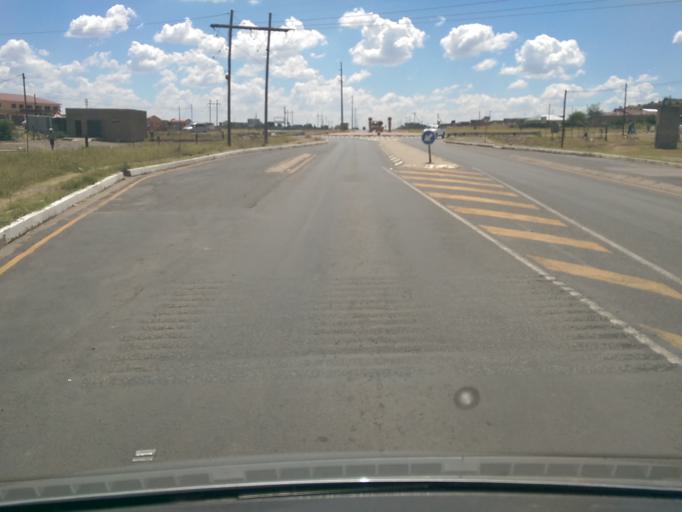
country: LS
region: Maseru
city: Maseru
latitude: -29.3654
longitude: 27.4702
